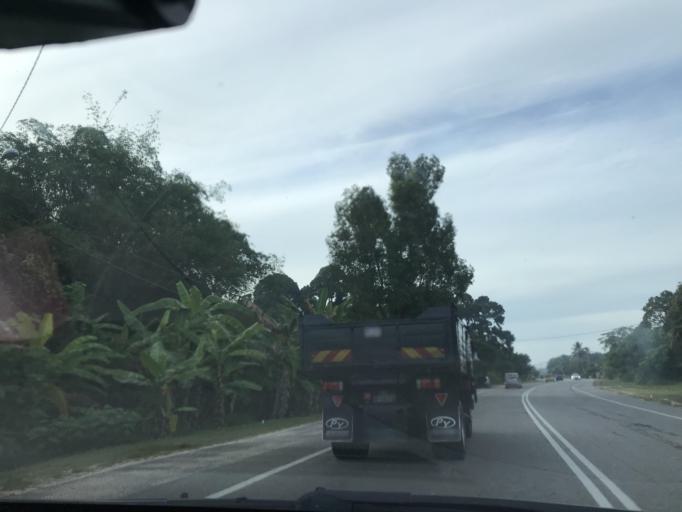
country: MY
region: Kelantan
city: Kampung Lemal
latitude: 6.0031
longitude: 102.1829
